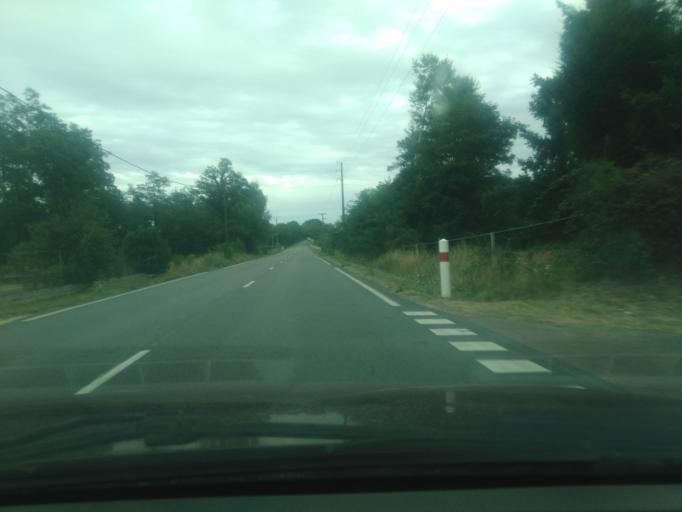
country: FR
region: Auvergne
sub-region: Departement de l'Allier
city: Ainay-le-Chateau
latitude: 46.7388
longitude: 2.6960
